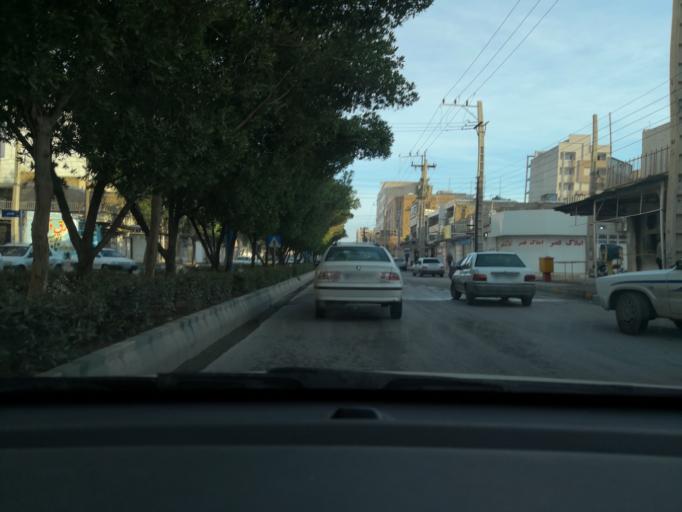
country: IR
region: Khuzestan
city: Ahvaz
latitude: 31.3527
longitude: 48.6773
